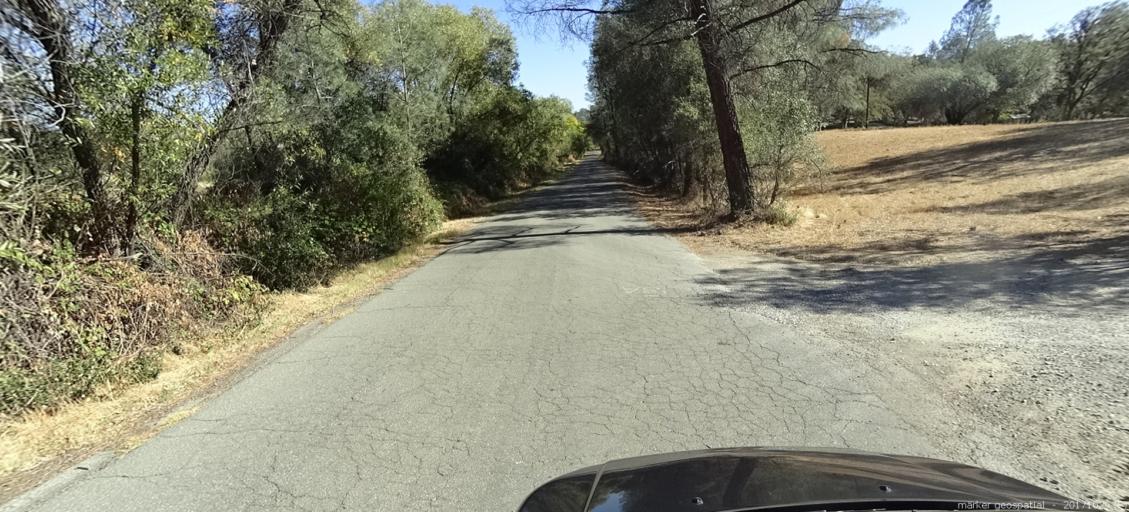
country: US
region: California
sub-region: Shasta County
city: Shasta
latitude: 40.4824
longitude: -122.6663
